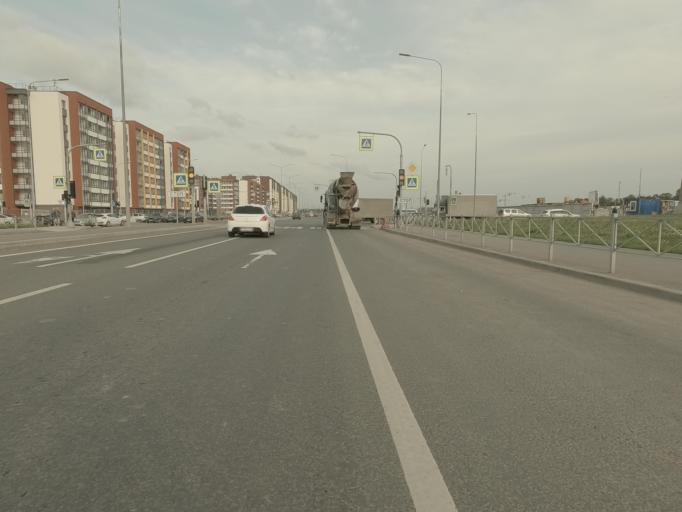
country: RU
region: St.-Petersburg
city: Sosnovaya Polyana
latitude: 59.8396
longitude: 30.0961
